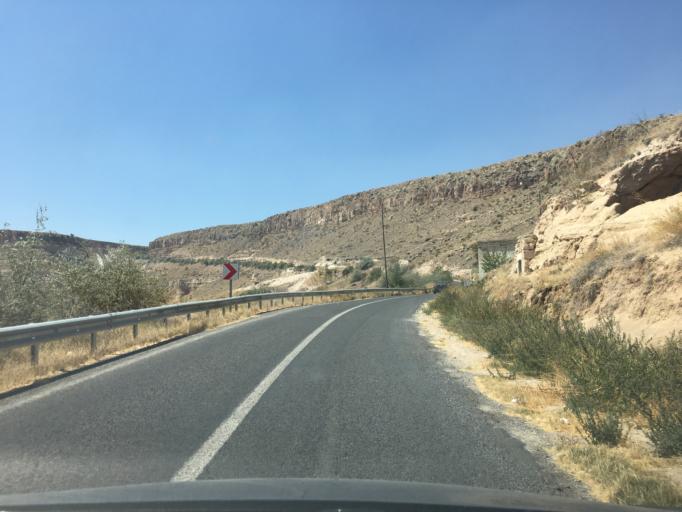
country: TR
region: Nevsehir
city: Urgub
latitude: 38.4697
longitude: 34.9447
